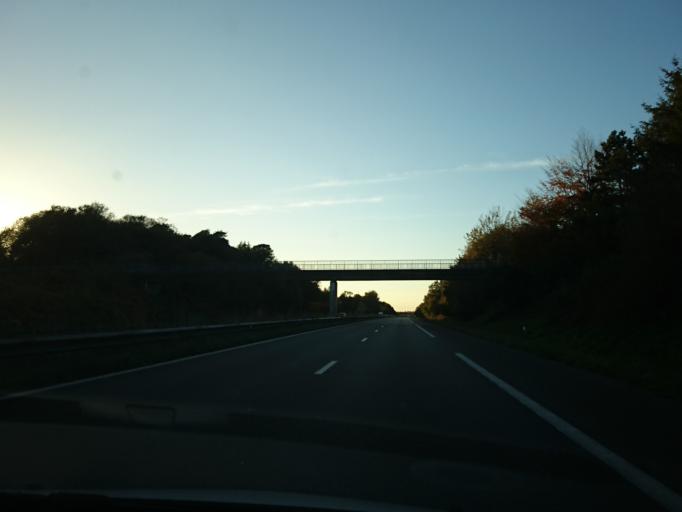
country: FR
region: Brittany
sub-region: Departement du Finistere
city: Plourin-les-Morlaix
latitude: 48.5841
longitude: -3.7685
